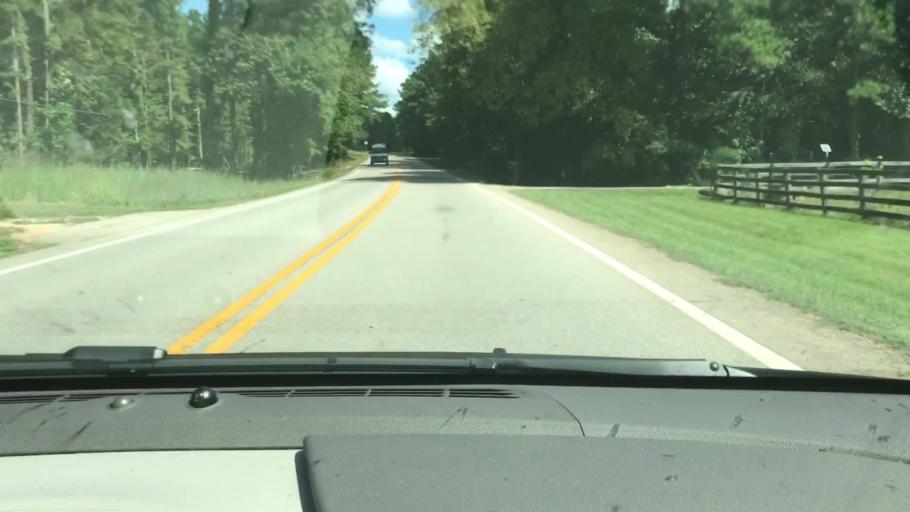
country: US
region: Georgia
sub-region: Troup County
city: La Grange
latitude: 32.9428
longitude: -85.0180
